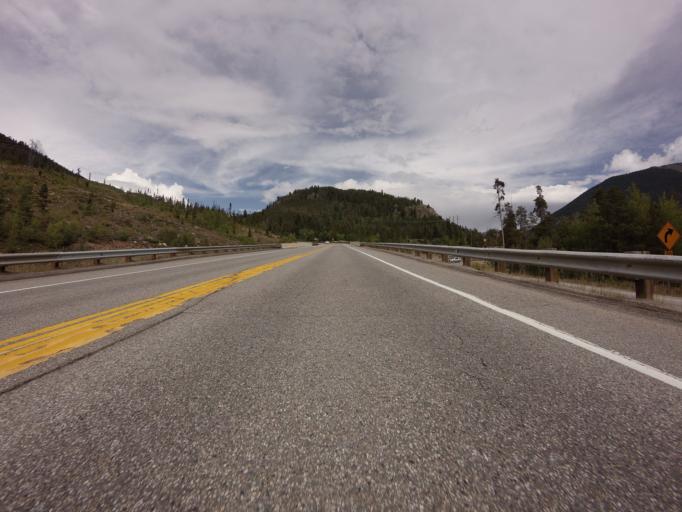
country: US
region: Colorado
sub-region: Summit County
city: Keystone
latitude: 39.6103
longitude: -105.9427
